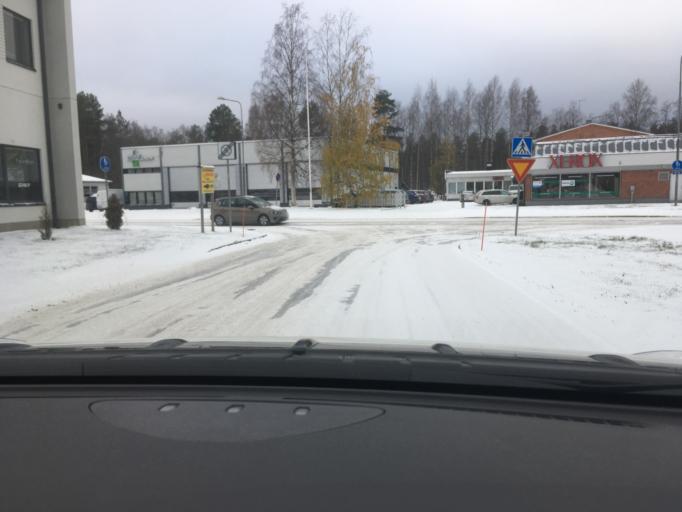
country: FI
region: North Karelia
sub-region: Joensuu
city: Joensuu
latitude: 62.6117
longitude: 29.7743
